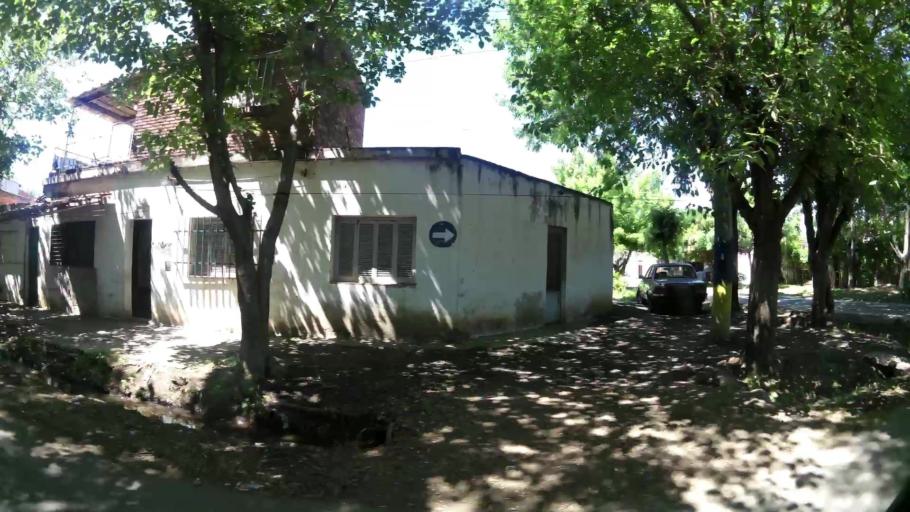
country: AR
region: Santa Fe
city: Perez
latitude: -32.9588
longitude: -60.7164
